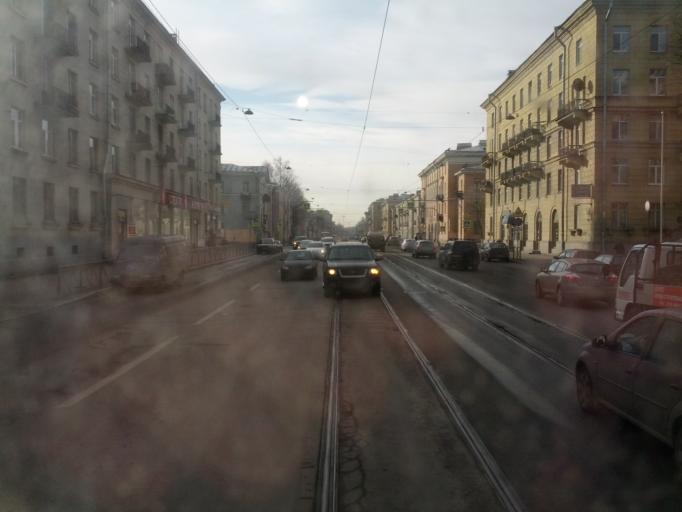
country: RU
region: Leningrad
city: Kalininskiy
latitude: 59.9585
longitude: 30.4156
